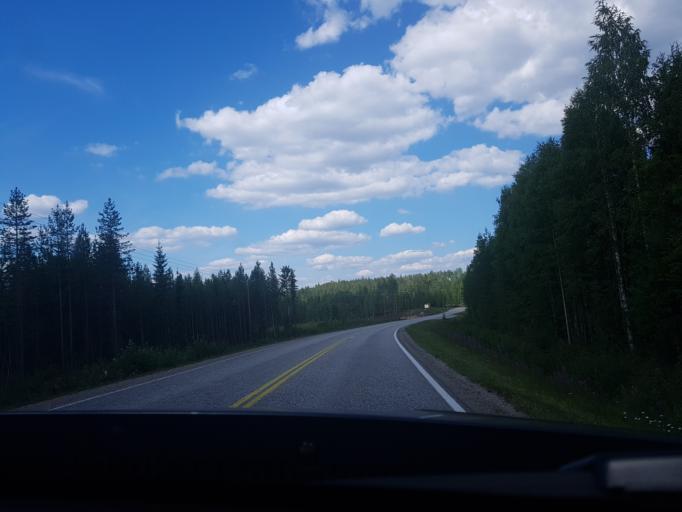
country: FI
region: Kainuu
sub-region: Kehys-Kainuu
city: Kuhmo
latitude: 64.2459
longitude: 29.8069
